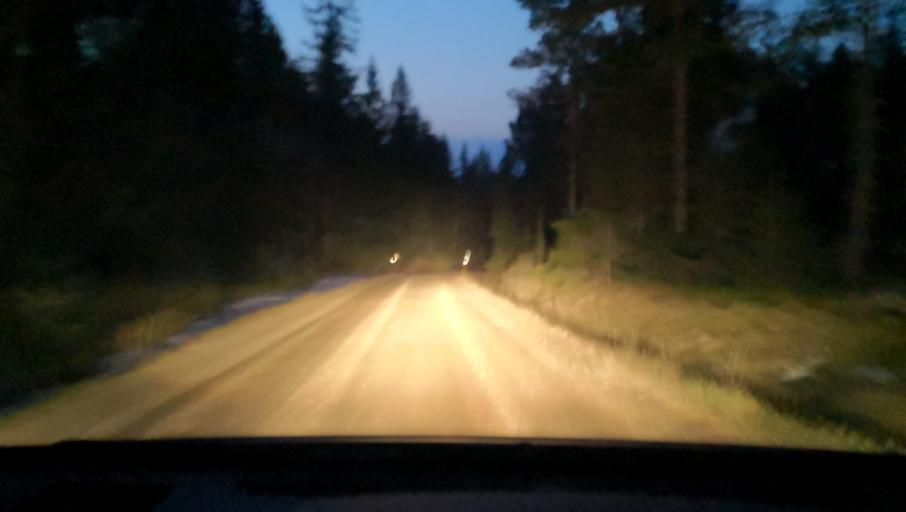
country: SE
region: OErebro
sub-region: Lindesbergs Kommun
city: Frovi
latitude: 59.6271
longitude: 15.4749
